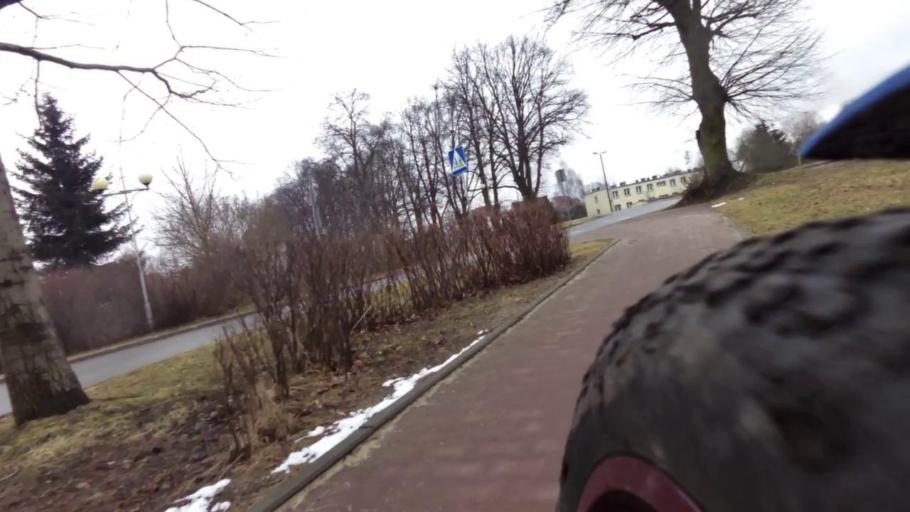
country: PL
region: West Pomeranian Voivodeship
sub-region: Powiat walecki
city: Walcz
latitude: 53.2776
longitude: 16.4583
